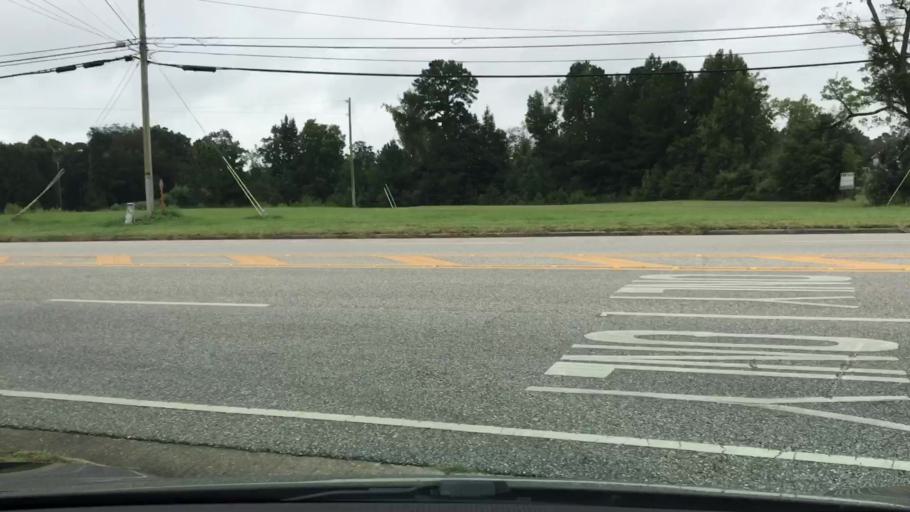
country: US
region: Alabama
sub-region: Coffee County
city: Elba
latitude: 31.4173
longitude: -86.0861
